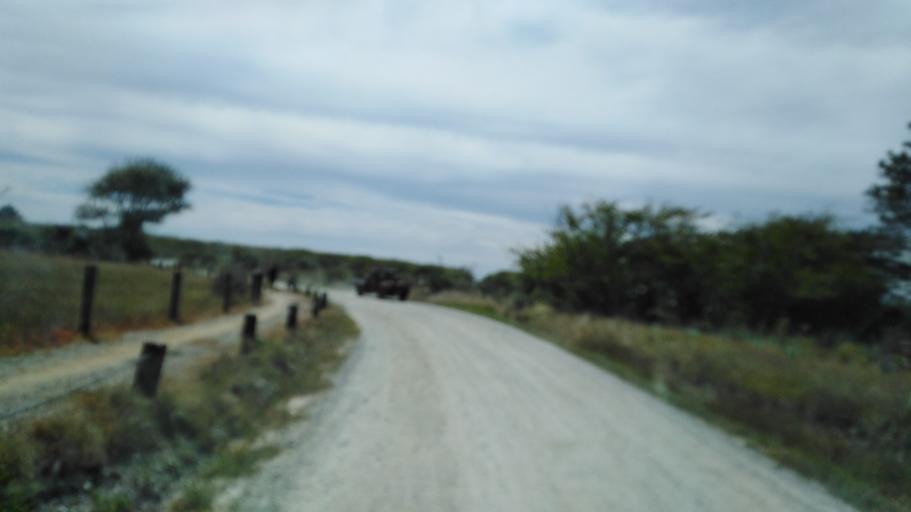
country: NZ
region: West Coast
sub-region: Buller District
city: Westport
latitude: -41.7378
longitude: 171.6044
